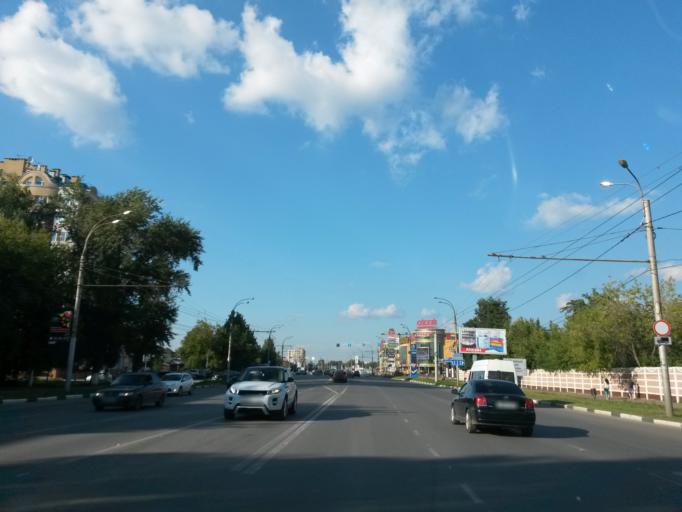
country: RU
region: Ivanovo
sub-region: Gorod Ivanovo
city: Ivanovo
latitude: 56.9797
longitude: 40.9784
